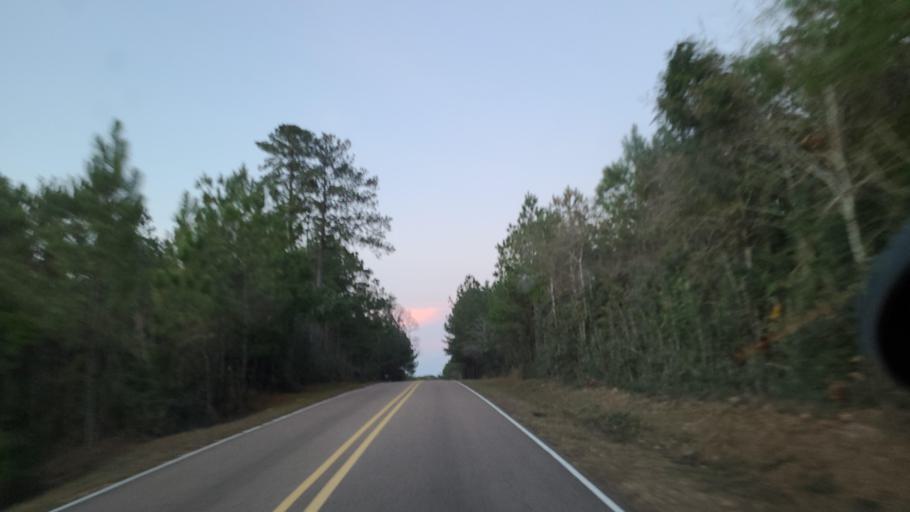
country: US
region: Mississippi
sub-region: Forrest County
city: Hattiesburg
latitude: 31.2171
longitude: -89.2376
